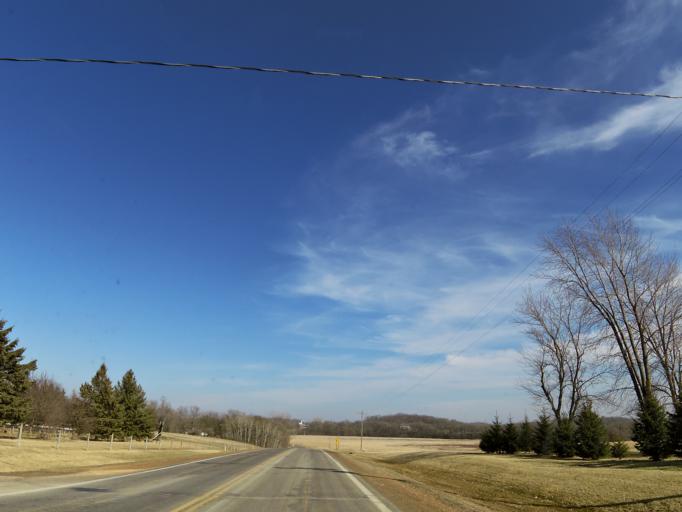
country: US
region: Minnesota
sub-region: Scott County
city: Prior Lake
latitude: 44.6306
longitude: -93.4543
